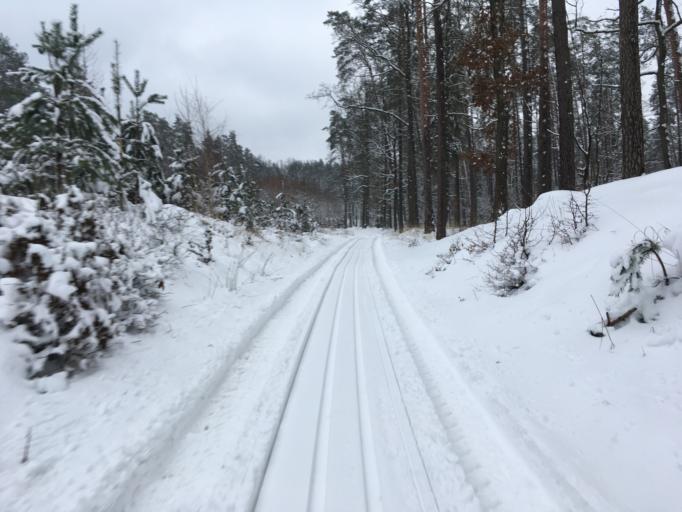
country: PL
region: Kujawsko-Pomorskie
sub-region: Powiat brodnicki
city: Gorzno
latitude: 53.1945
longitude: 19.6777
